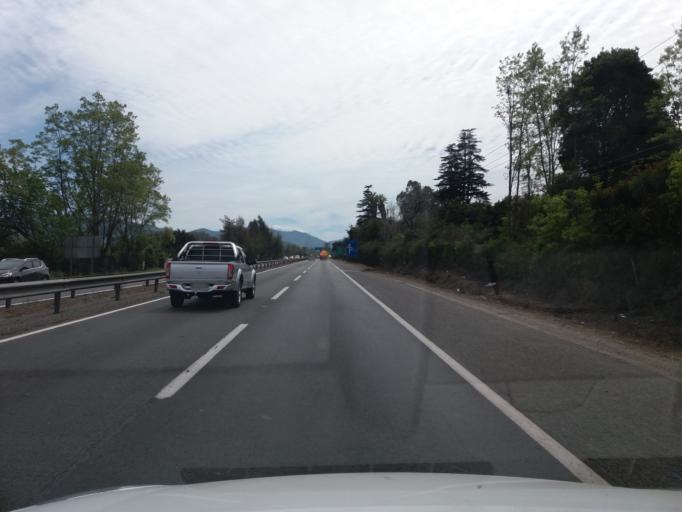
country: CL
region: Valparaiso
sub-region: Provincia de Quillota
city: Hacienda La Calera
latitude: -32.7284
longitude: -71.2019
